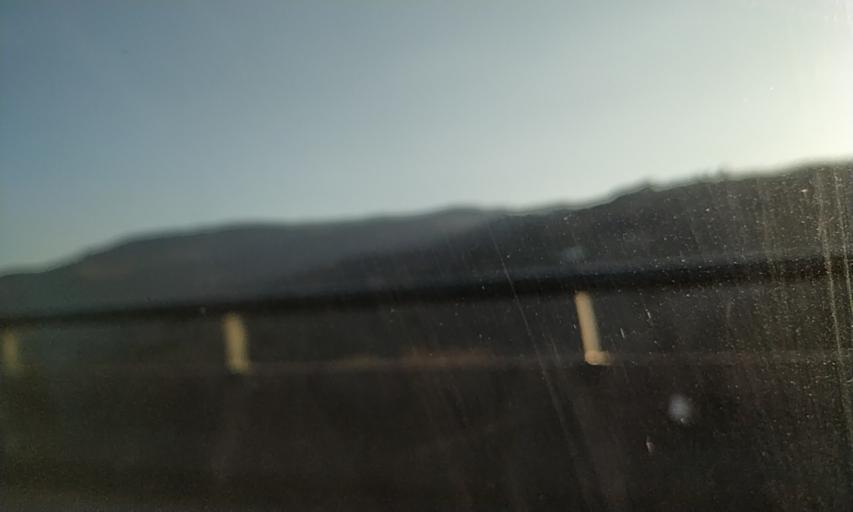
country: ES
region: Galicia
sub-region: Provincia de Lugo
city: Becerrea
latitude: 42.8408
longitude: -7.1182
